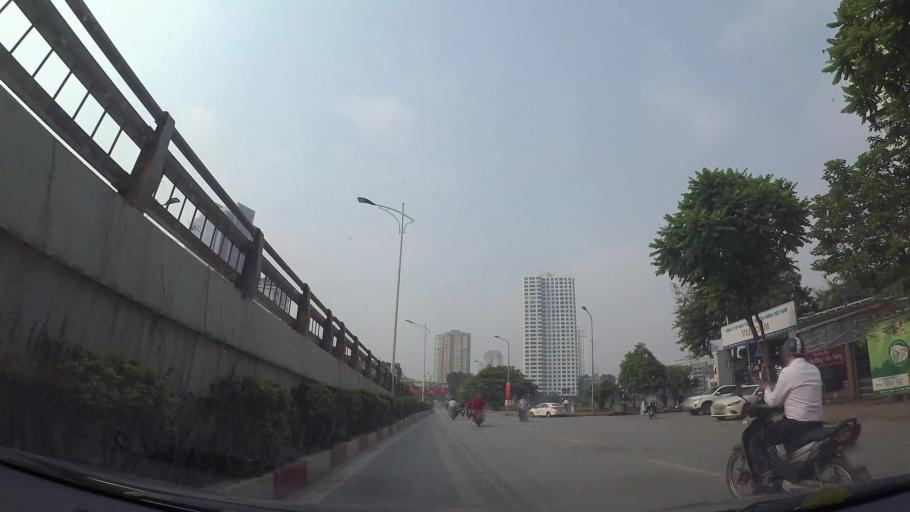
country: VN
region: Ha Noi
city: Cau Giay
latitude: 21.0291
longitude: 105.8124
